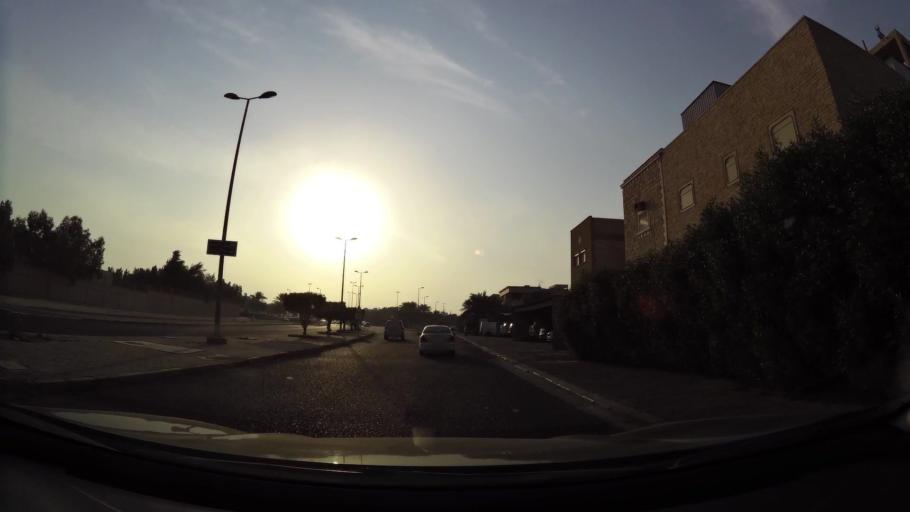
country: KW
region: Mubarak al Kabir
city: Sabah as Salim
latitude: 29.2499
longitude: 48.0693
